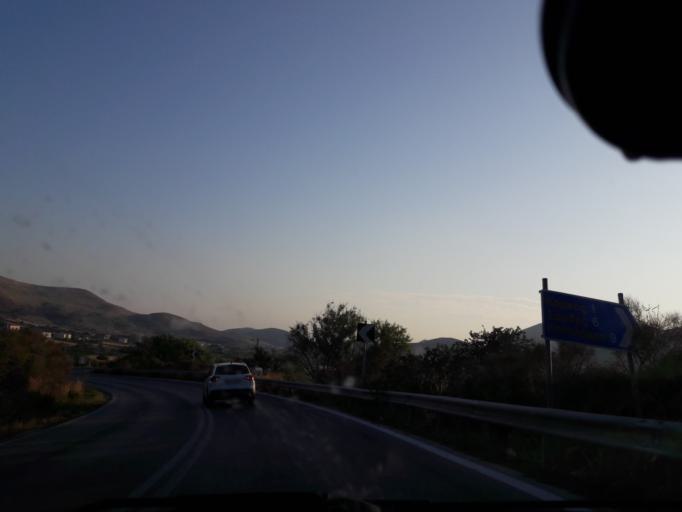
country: GR
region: North Aegean
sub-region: Nomos Lesvou
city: Myrina
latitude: 39.9119
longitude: 25.1126
